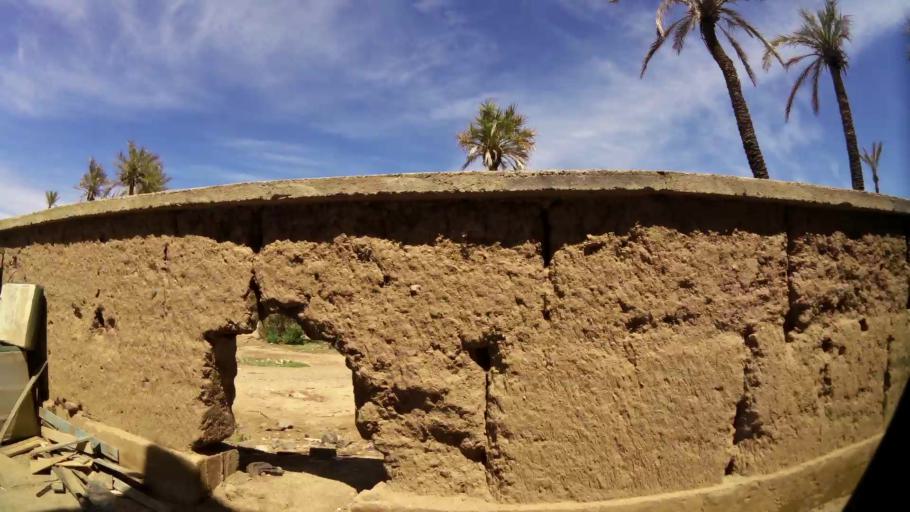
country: MA
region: Marrakech-Tensift-Al Haouz
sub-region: Marrakech
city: Marrakesh
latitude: 31.6669
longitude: -7.9865
